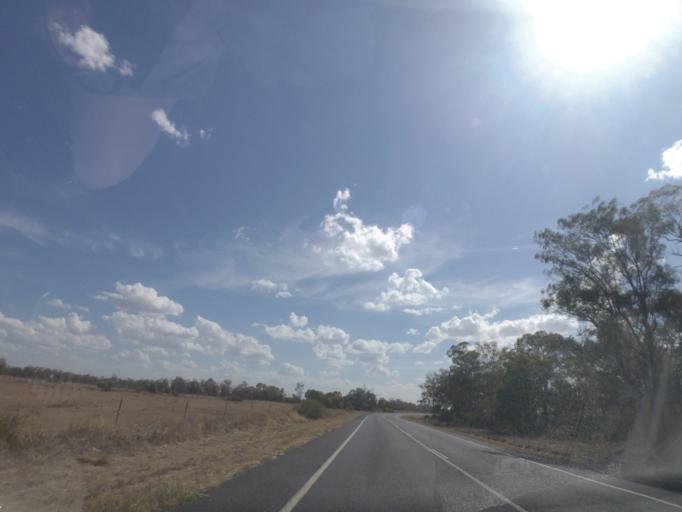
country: AU
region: Queensland
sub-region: Southern Downs
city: Stanthorpe
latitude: -28.4126
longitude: 151.1661
